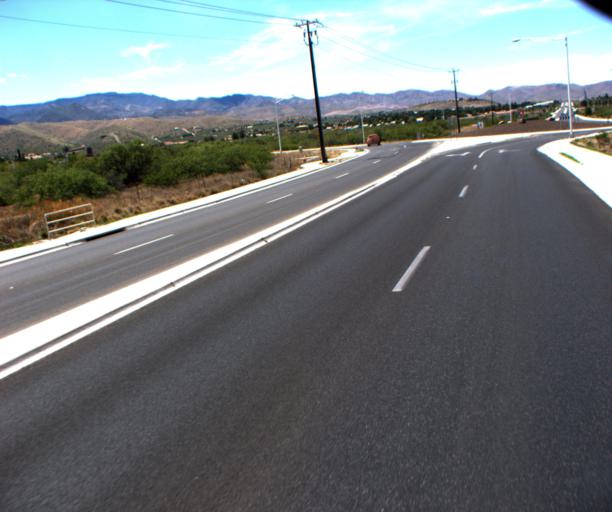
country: US
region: Arizona
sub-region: Yavapai County
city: Clarkdale
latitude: 34.7464
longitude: -112.0442
